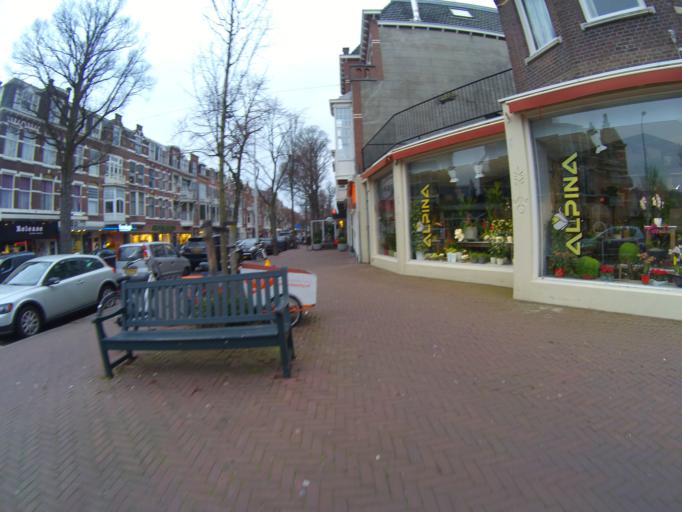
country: NL
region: South Holland
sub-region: Gemeente Den Haag
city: Scheveningen
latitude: 52.0892
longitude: 4.2752
